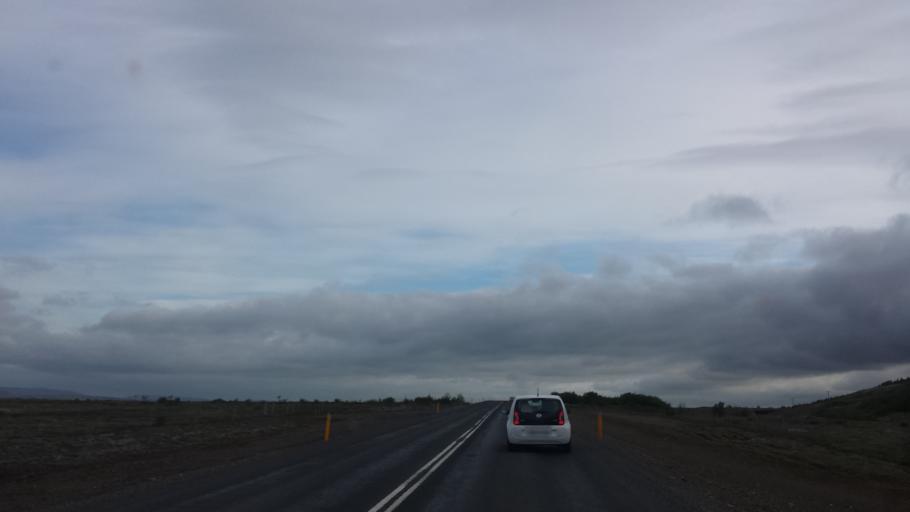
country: IS
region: South
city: Selfoss
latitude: 64.2889
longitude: -20.3385
